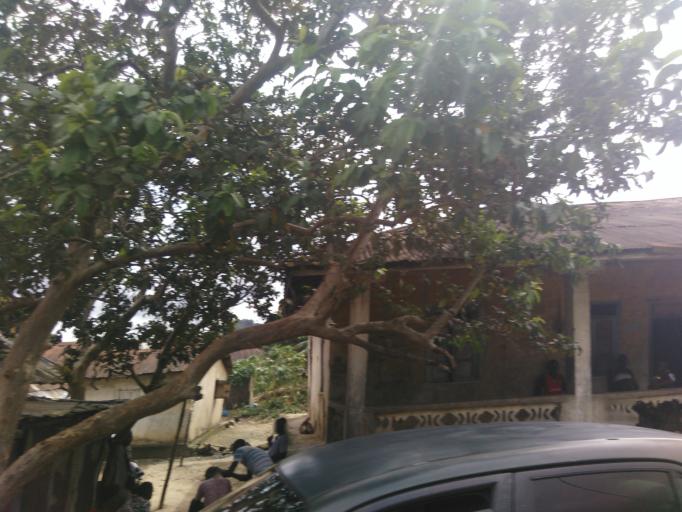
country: SL
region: Northern Province
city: Makali
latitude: 8.6291
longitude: -11.6621
